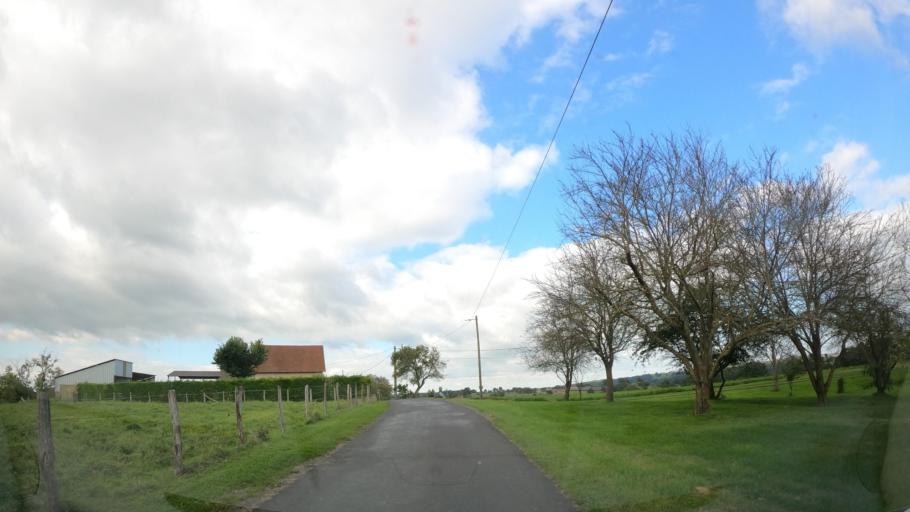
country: FR
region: Auvergne
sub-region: Departement de l'Allier
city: Lapalisse
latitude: 46.3641
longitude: 3.6214
